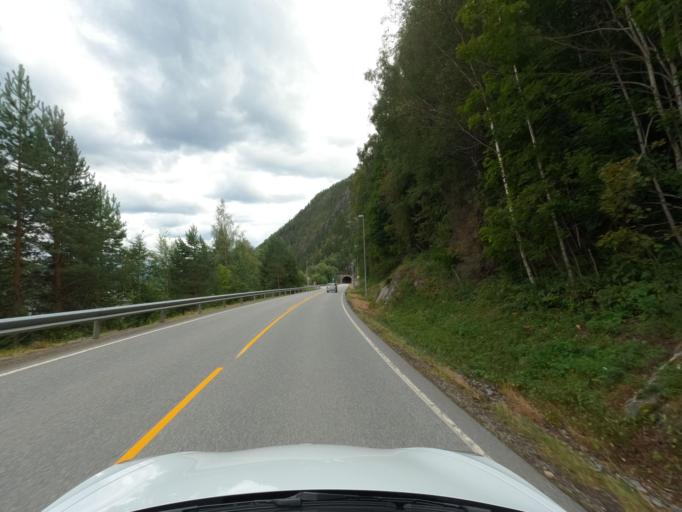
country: NO
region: Telemark
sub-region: Hjartdal
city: Sauland
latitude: 59.8777
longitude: 8.9165
